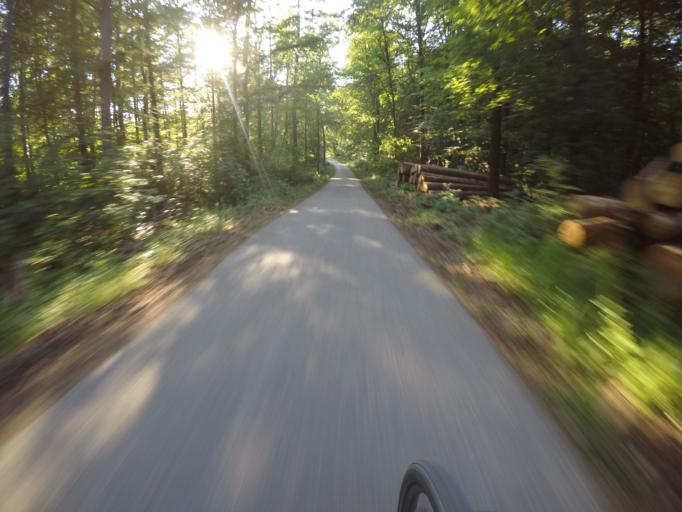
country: DE
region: Baden-Wuerttemberg
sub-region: Regierungsbezirk Stuttgart
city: Fellbach
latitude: 48.7841
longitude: 9.3051
